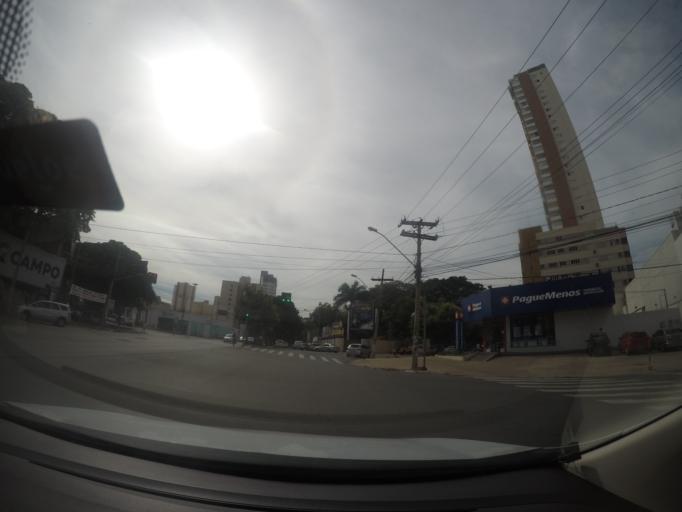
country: BR
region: Goias
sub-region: Goiania
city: Goiania
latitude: -16.6779
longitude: -49.2646
